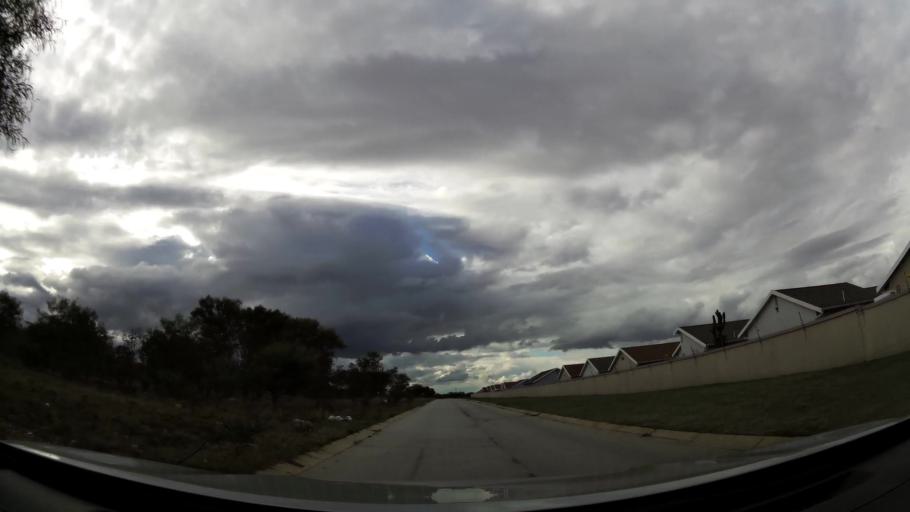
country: ZA
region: Eastern Cape
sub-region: Nelson Mandela Bay Metropolitan Municipality
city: Port Elizabeth
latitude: -33.9308
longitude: 25.4644
